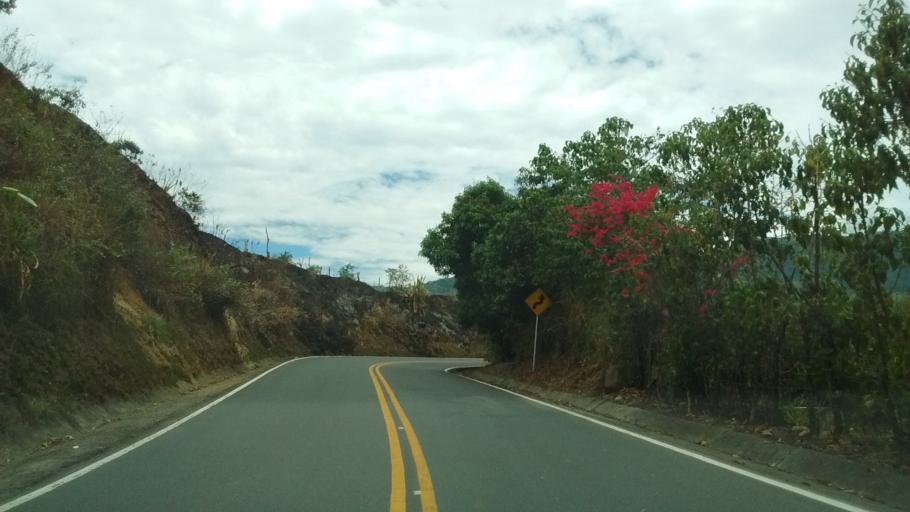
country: CO
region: Cauca
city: La Sierra
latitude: 2.2291
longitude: -76.7950
